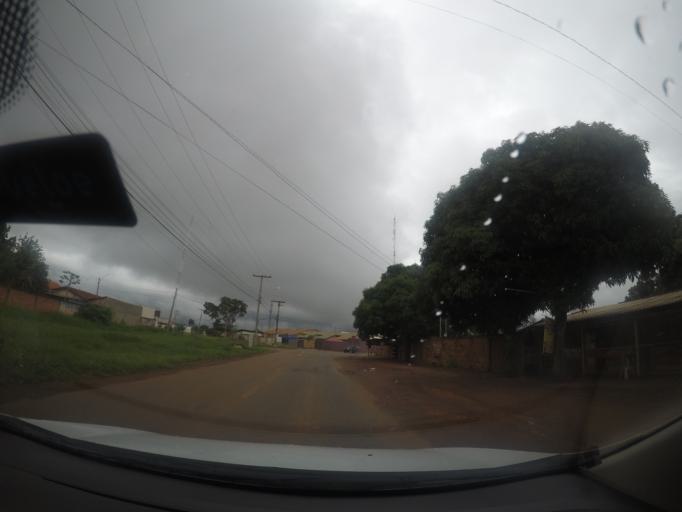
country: BR
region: Goias
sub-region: Trindade
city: Trindade
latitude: -16.6139
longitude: -49.3922
